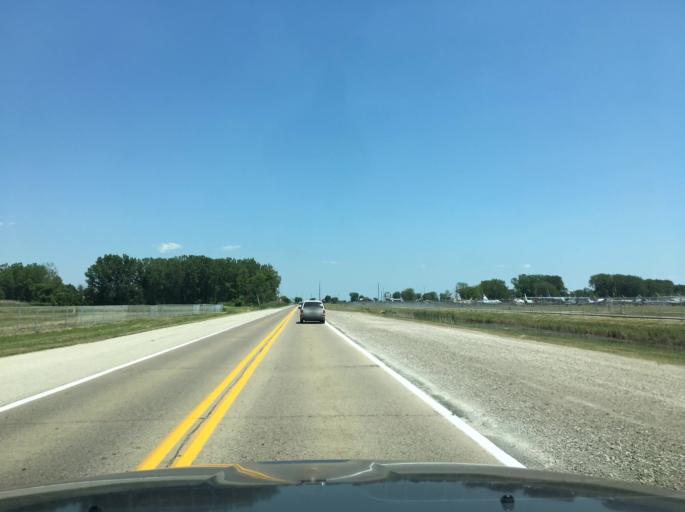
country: US
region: Michigan
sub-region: Macomb County
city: Mount Clemens
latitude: 42.6305
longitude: -82.8341
